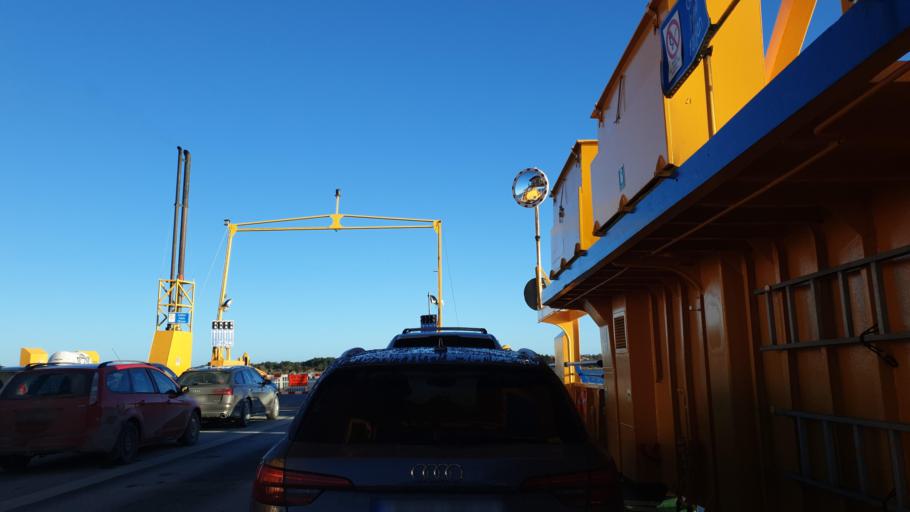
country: SE
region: Gotland
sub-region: Gotland
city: Slite
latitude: 57.8672
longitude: 19.0737
